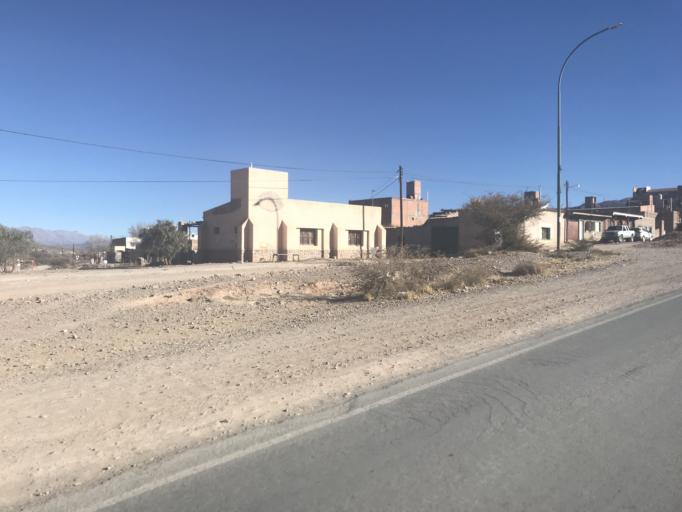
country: AR
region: Jujuy
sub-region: Departamento de Humahuaca
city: Humahuaca
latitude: -23.2147
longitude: -65.3493
